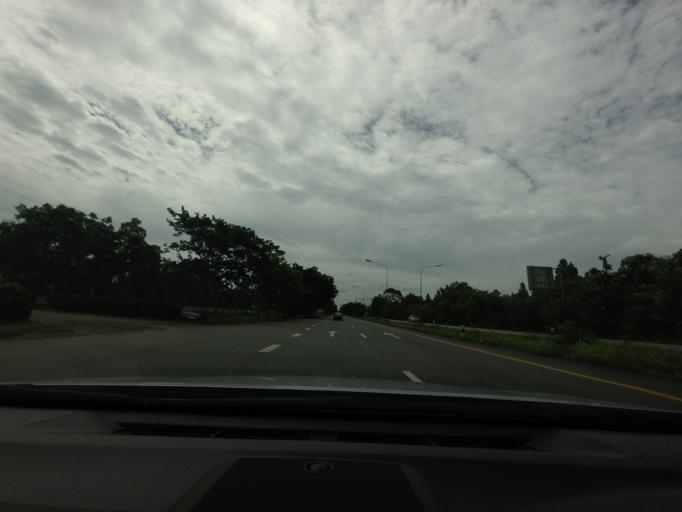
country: TH
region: Chumphon
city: Lamae
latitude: 9.7291
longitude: 99.1028
